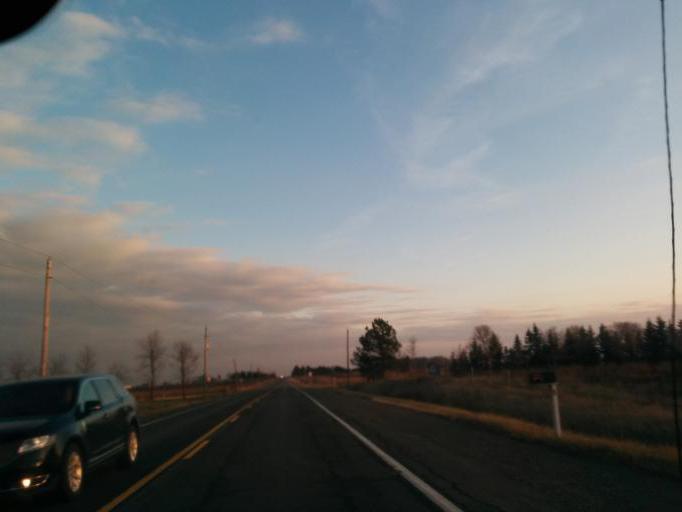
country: CA
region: Ontario
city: Brampton
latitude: 43.8507
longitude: -79.7697
